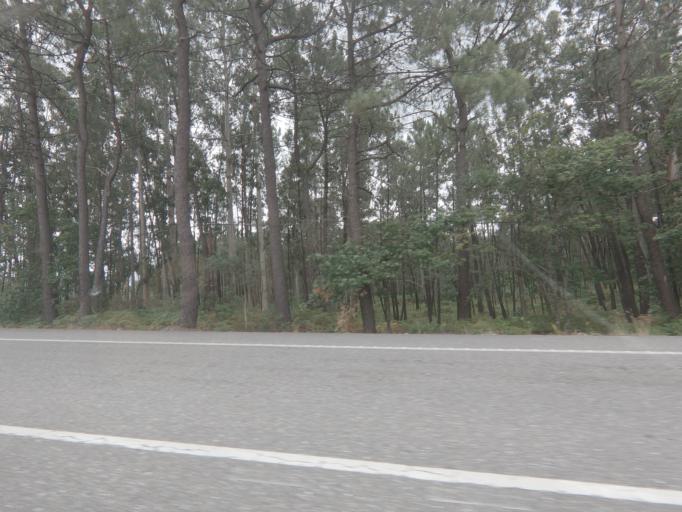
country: PT
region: Viana do Castelo
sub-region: Vila Nova de Cerveira
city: Vila Nova de Cerveira
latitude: 41.9413
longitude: -8.7826
